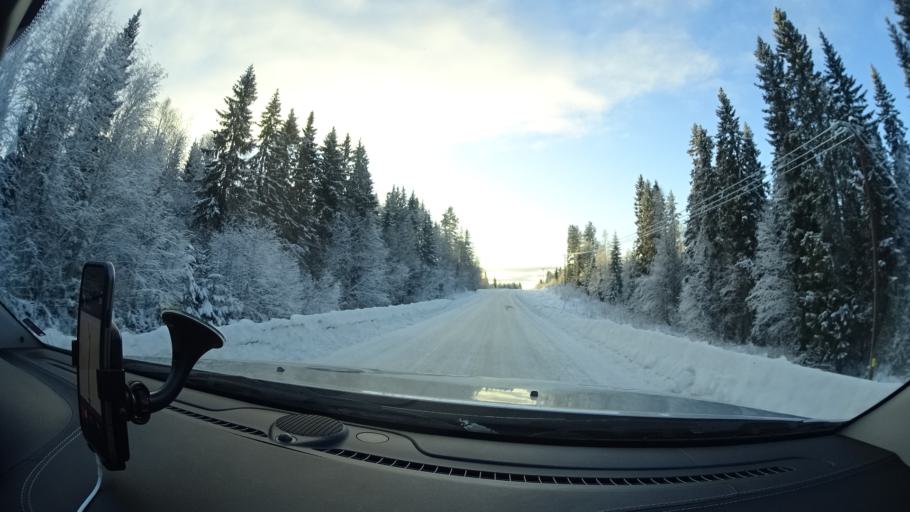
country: SE
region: Jaemtland
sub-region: Ragunda Kommun
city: Hammarstrand
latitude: 63.2114
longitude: 15.9526
